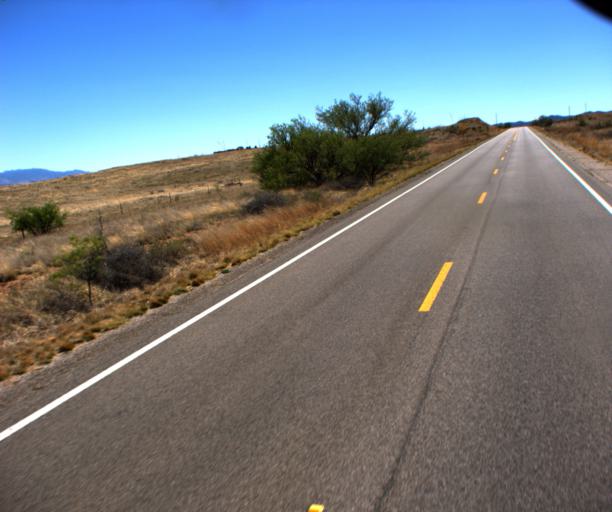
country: US
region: Arizona
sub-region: Pima County
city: Corona de Tucson
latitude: 31.7014
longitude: -110.6554
